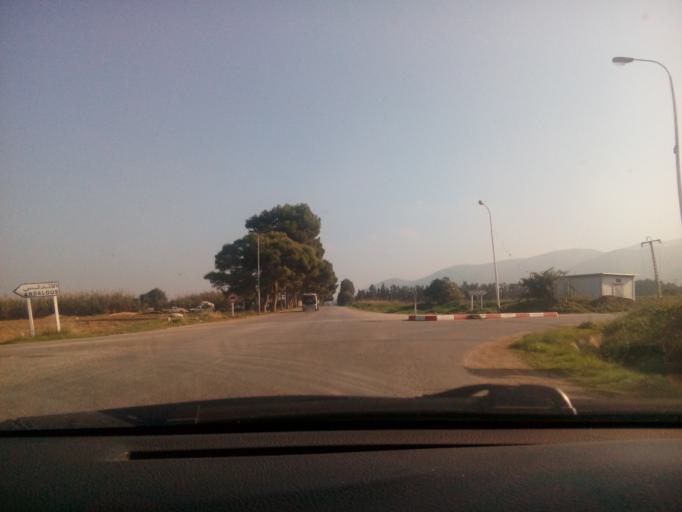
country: DZ
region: Oran
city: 'Ain el Turk
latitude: 35.7001
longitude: -0.8768
